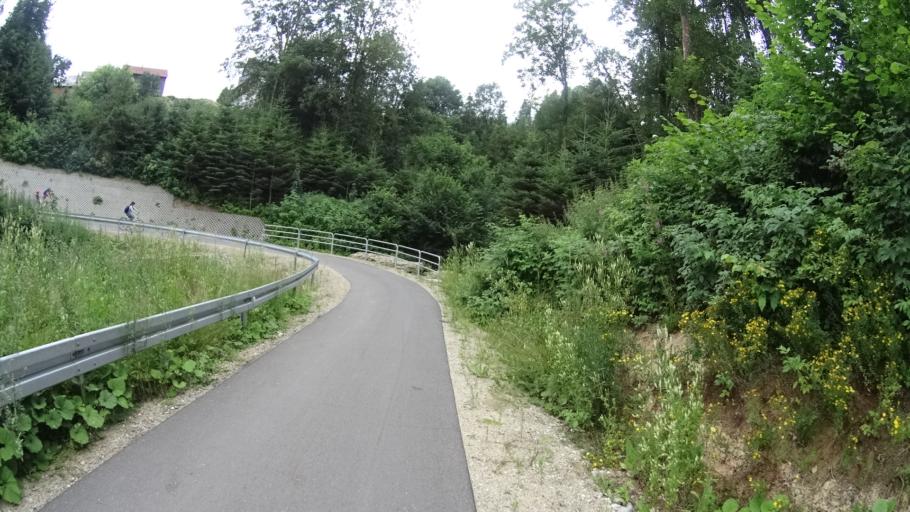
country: PL
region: Lesser Poland Voivodeship
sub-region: Powiat nowotarski
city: Niedzica
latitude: 49.4250
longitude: 20.3071
